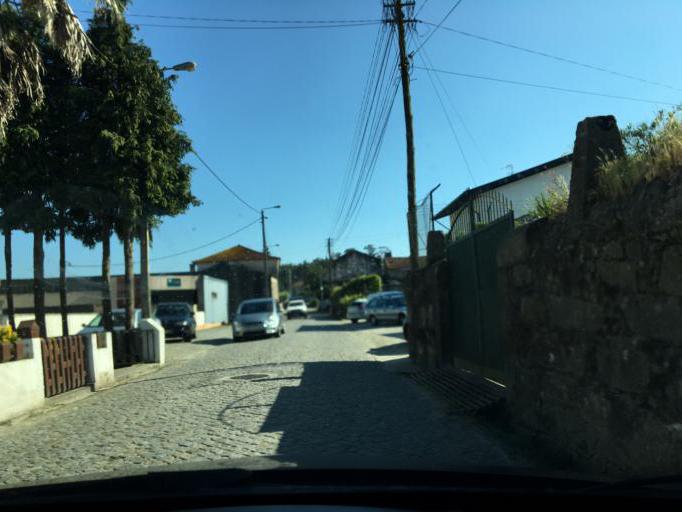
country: PT
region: Porto
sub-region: Maia
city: Anta
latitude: 41.2713
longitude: -8.6181
